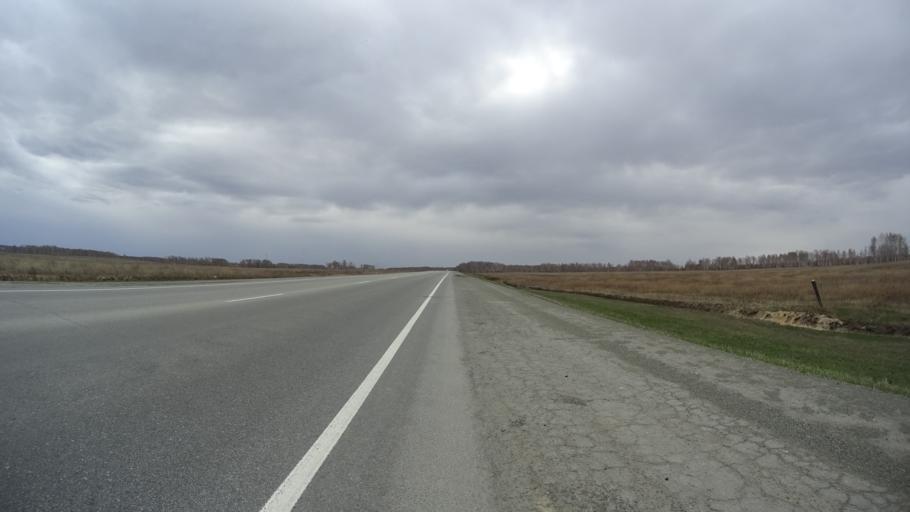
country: RU
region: Chelyabinsk
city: Yemanzhelinsk
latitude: 54.7047
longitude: 61.2556
